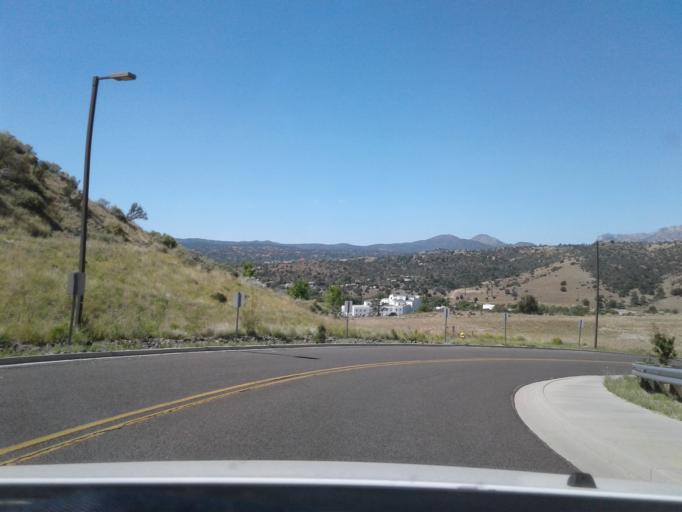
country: US
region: Arizona
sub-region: Yavapai County
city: Prescott
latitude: 34.5527
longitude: -112.4472
